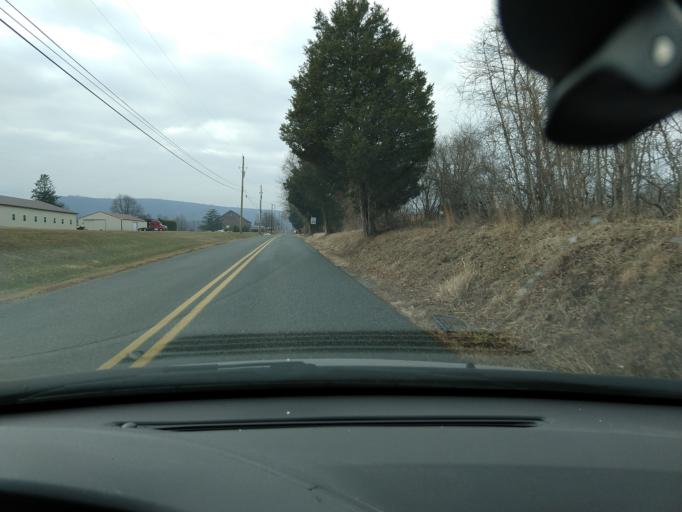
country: US
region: Pennsylvania
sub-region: Berks County
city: Amity Gardens
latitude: 40.2482
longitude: -75.7406
